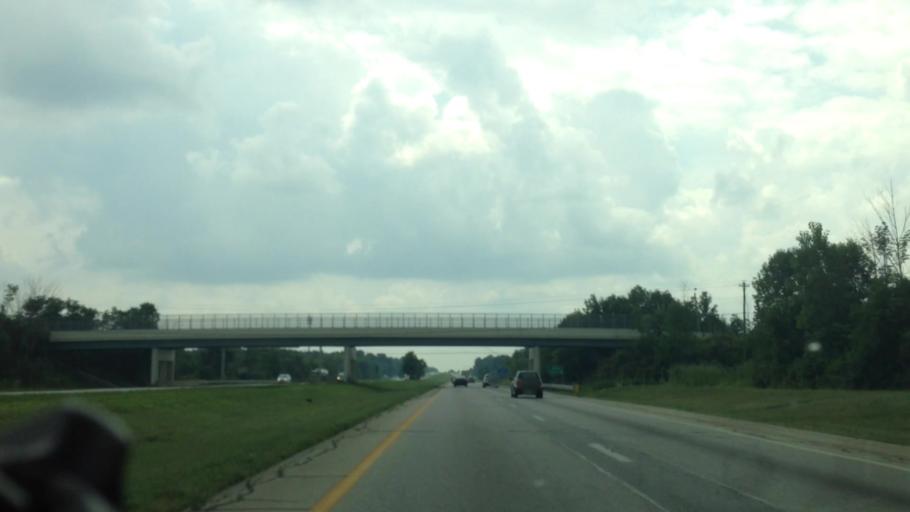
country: US
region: Ohio
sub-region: Summit County
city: Richfield
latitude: 41.2036
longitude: -81.6258
